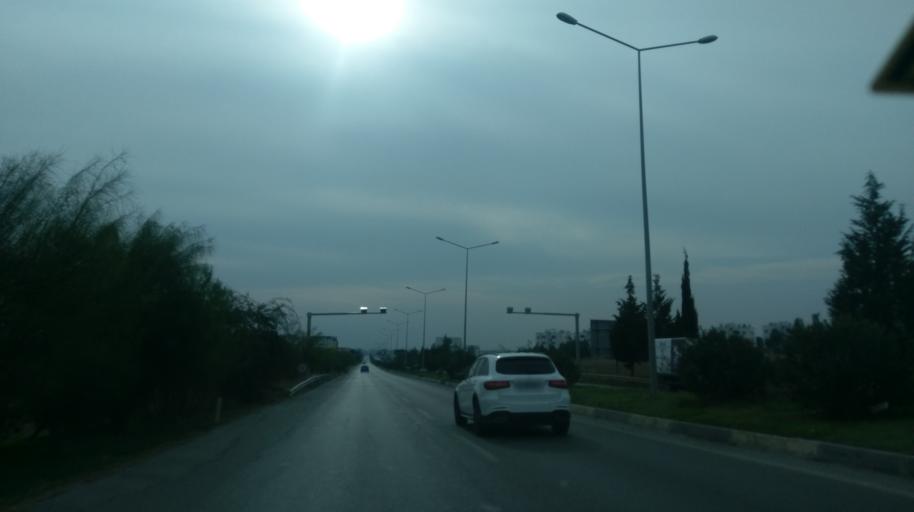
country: CY
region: Keryneia
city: Kyrenia
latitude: 35.2814
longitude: 33.2824
